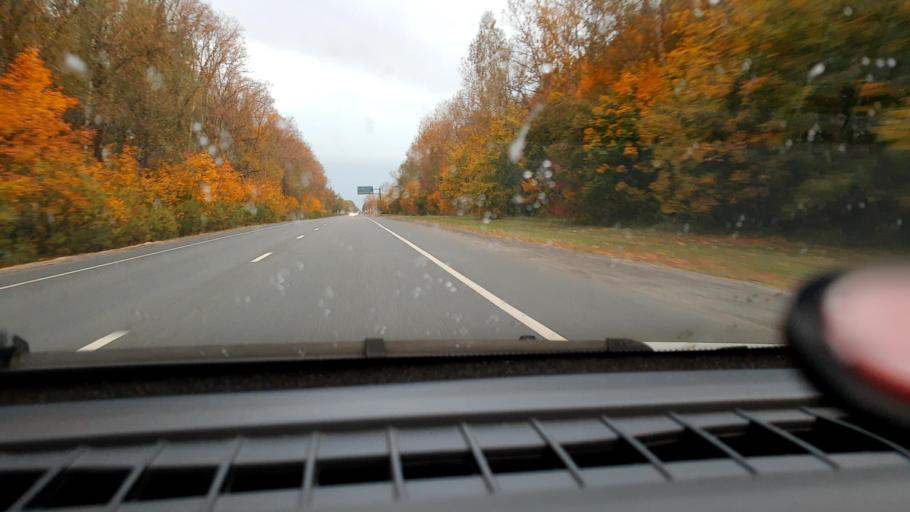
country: RU
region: Vladimir
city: Orgtrud
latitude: 56.2026
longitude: 40.7684
